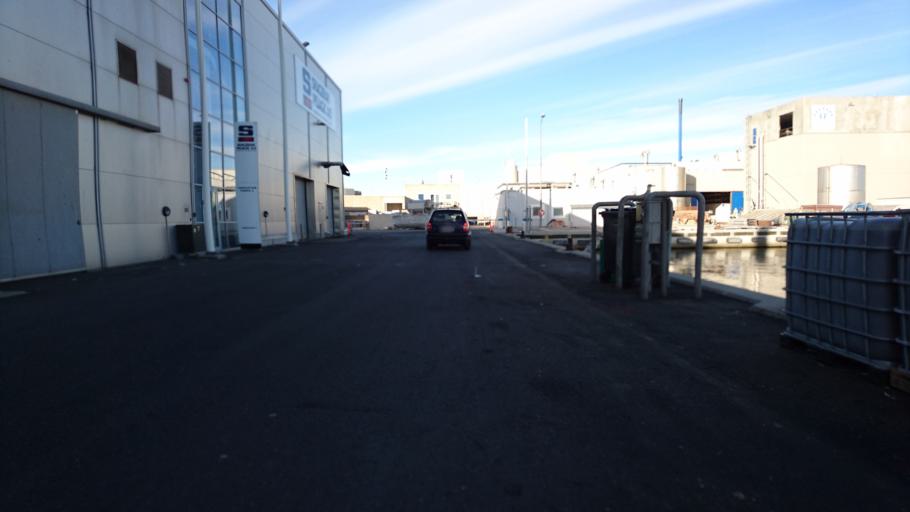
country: DK
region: North Denmark
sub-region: Frederikshavn Kommune
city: Skagen
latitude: 57.7188
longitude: 10.5960
